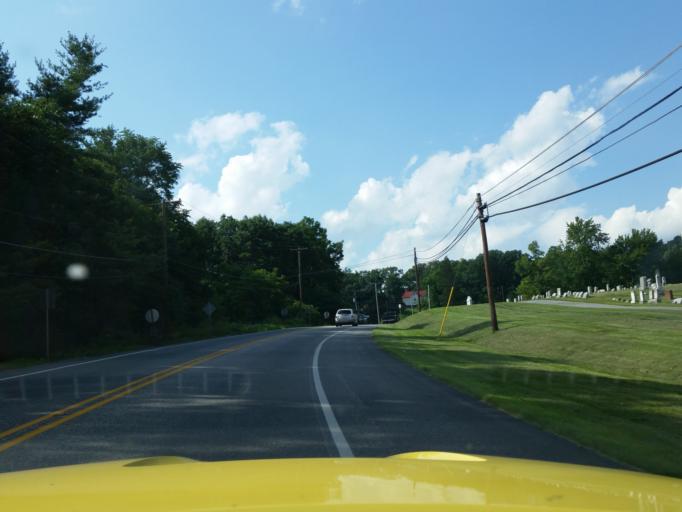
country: US
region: Pennsylvania
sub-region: Lebanon County
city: Annville
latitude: 40.3357
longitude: -76.5194
